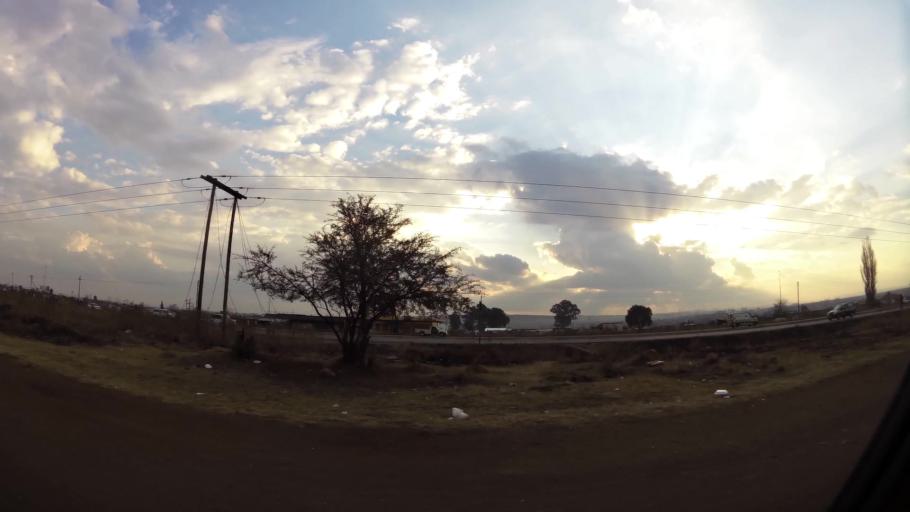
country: ZA
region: Gauteng
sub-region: City of Johannesburg Metropolitan Municipality
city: Orange Farm
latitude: -26.5556
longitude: 27.8303
